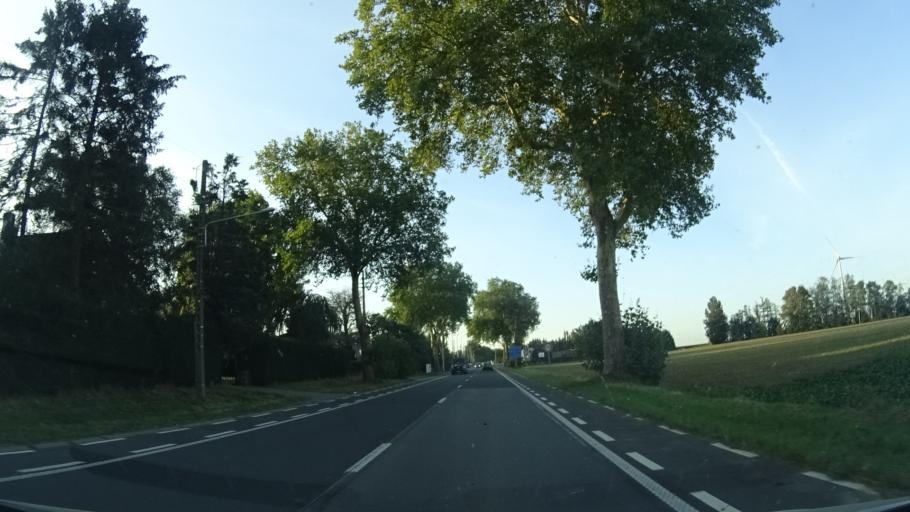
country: BE
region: Wallonia
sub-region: Province du Hainaut
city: Chasse Royale
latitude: 50.3949
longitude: 3.9644
